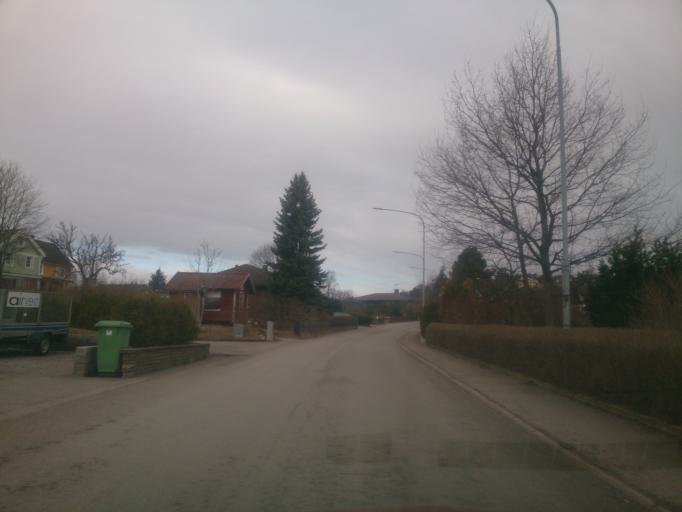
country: SE
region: OEstergoetland
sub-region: Norrkopings Kommun
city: Jursla
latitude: 58.6705
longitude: 16.1877
